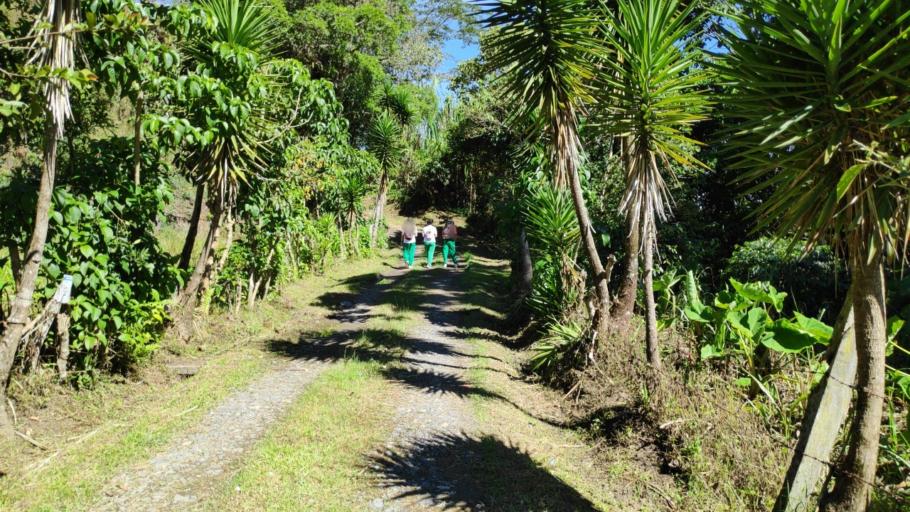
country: CO
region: Santander
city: Guepsa
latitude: 5.9883
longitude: -73.5421
